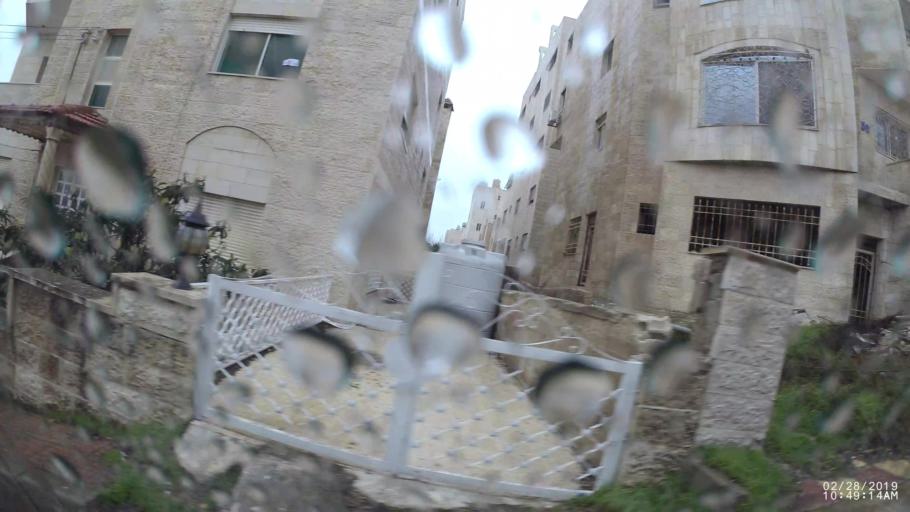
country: JO
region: Amman
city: Al Jubayhah
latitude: 32.0131
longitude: 35.8915
